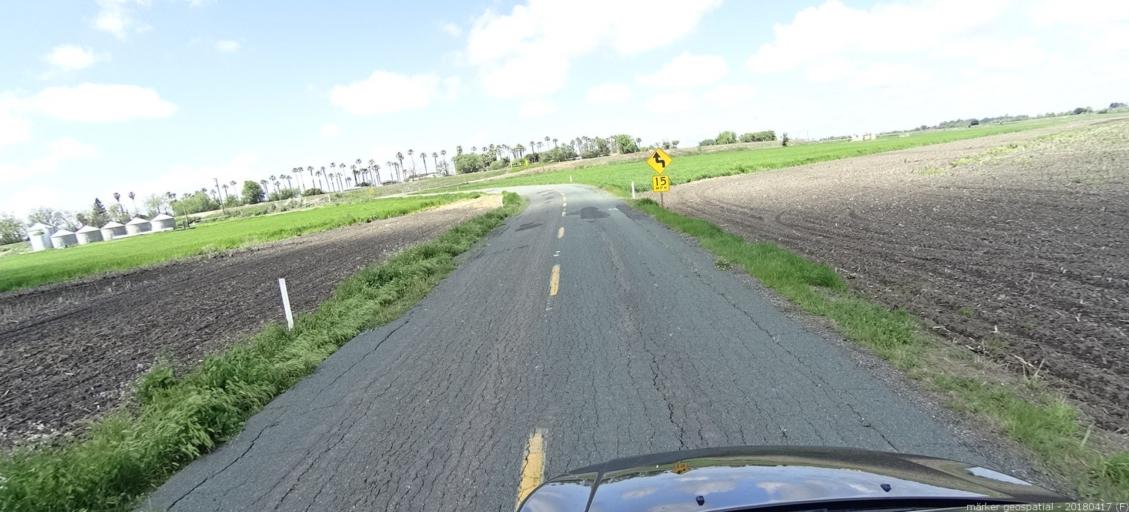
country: US
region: California
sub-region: Solano County
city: Rio Vista
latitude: 38.1468
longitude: -121.5844
